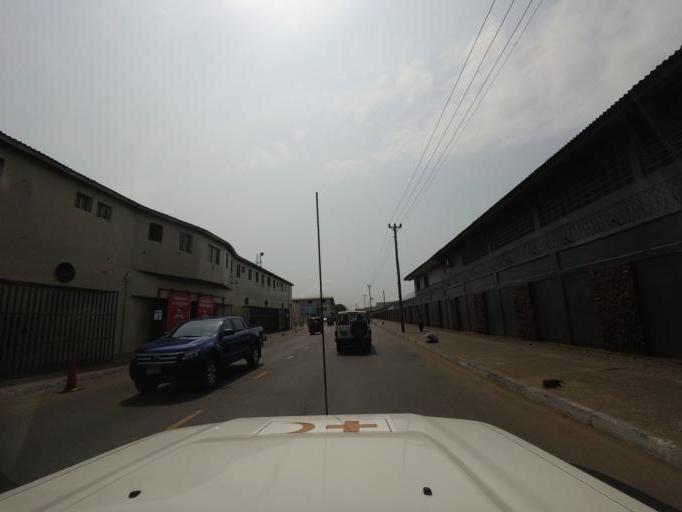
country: LR
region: Montserrado
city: Monrovia
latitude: 6.3086
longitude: -10.8047
